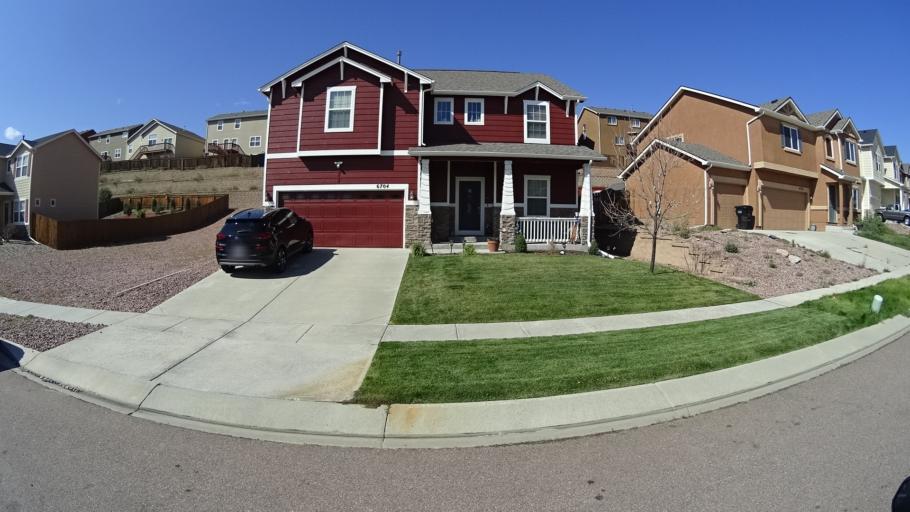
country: US
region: Colorado
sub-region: El Paso County
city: Cimarron Hills
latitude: 38.9287
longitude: -104.7064
